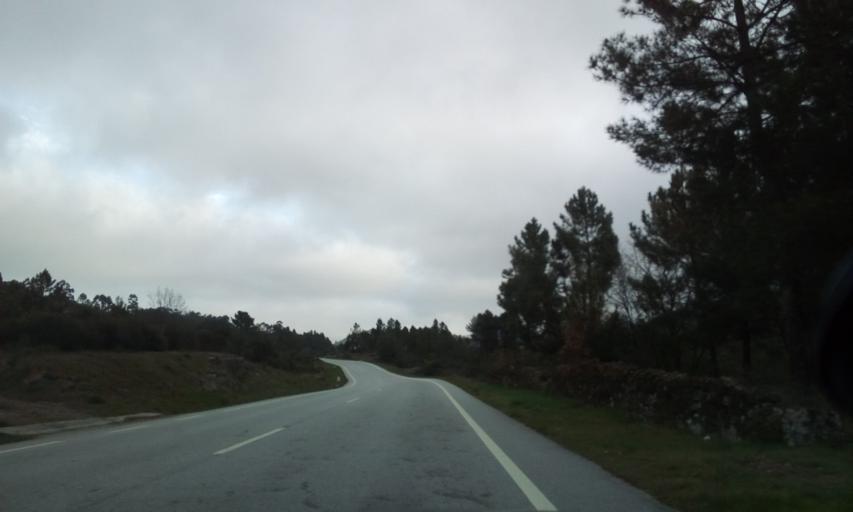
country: PT
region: Guarda
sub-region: Fornos de Algodres
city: Fornos de Algodres
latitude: 40.6432
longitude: -7.4924
